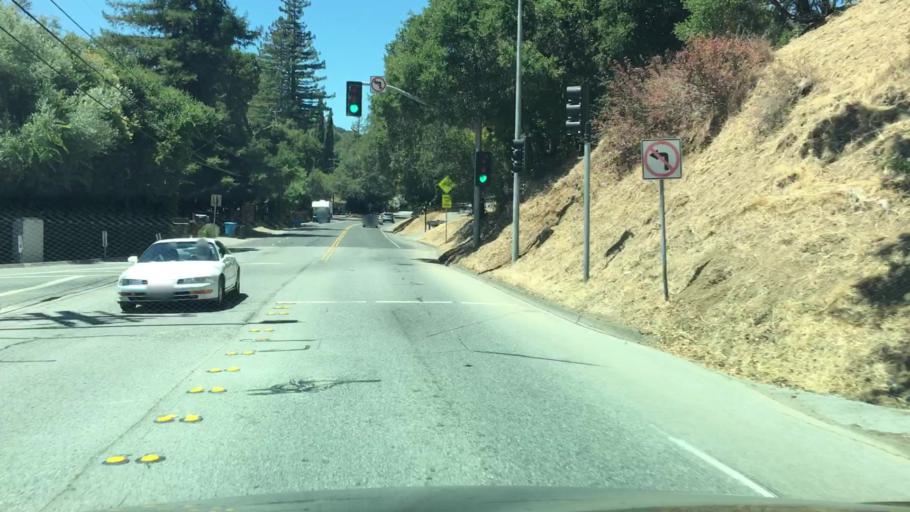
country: US
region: California
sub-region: San Mateo County
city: Emerald Lake Hills
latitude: 37.4747
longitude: -122.2732
